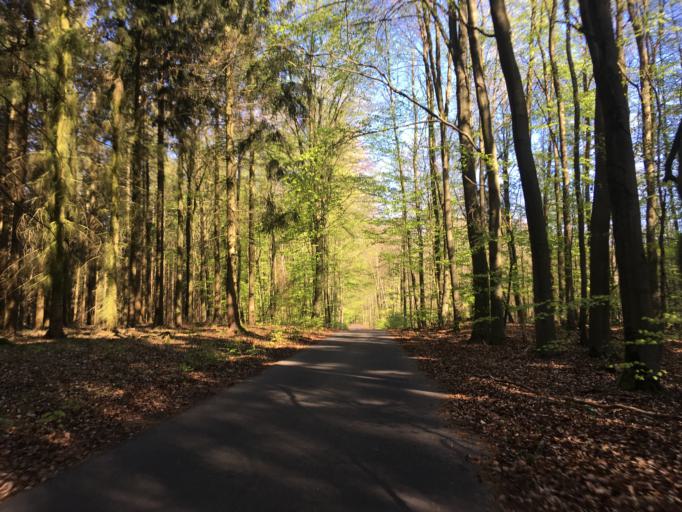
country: DE
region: Brandenburg
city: Wandlitz
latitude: 52.7339
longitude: 13.5034
